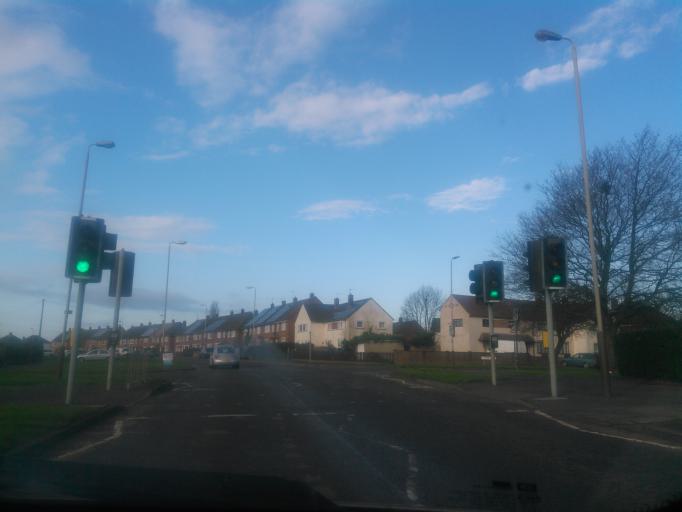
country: GB
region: England
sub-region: Leicestershire
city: Glenfield
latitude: 52.6434
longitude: -1.1852
